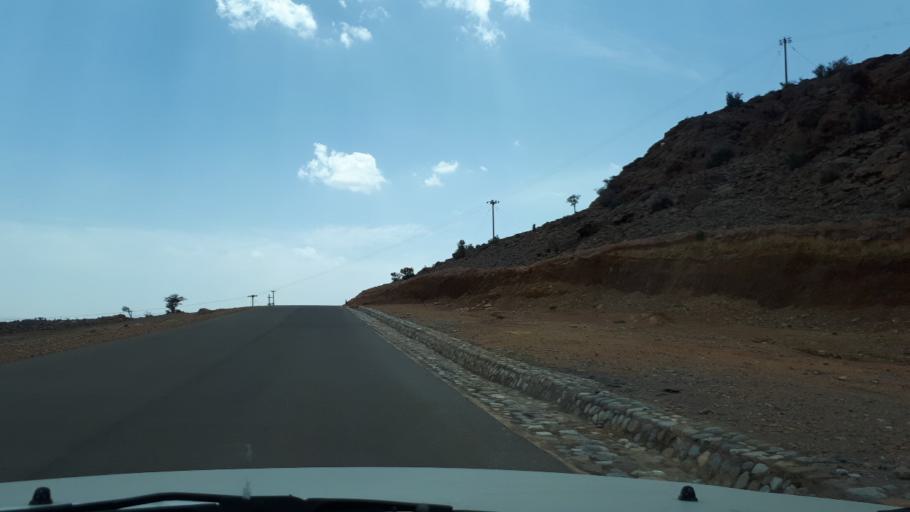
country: OM
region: Muhafazat ad Dakhiliyah
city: Bahla'
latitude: 23.2219
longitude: 57.2032
